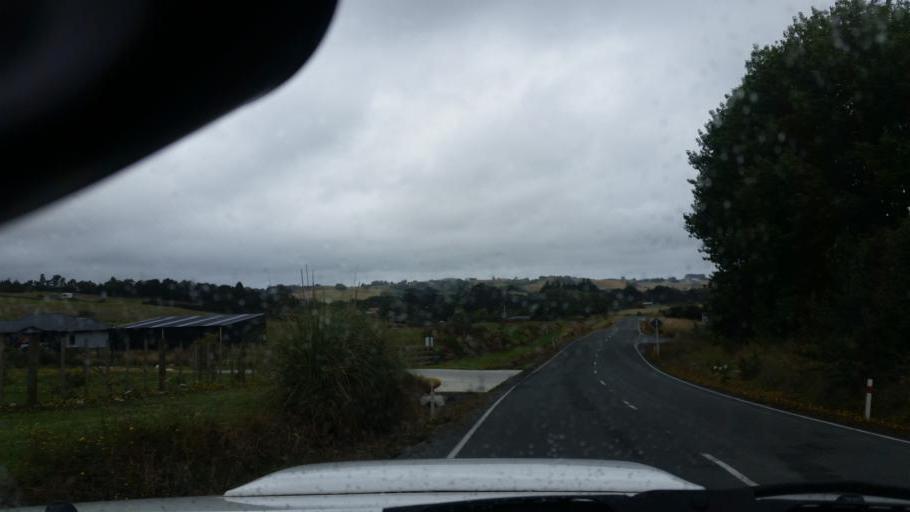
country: NZ
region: Auckland
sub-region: Auckland
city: Wellsford
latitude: -36.1416
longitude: 174.5010
